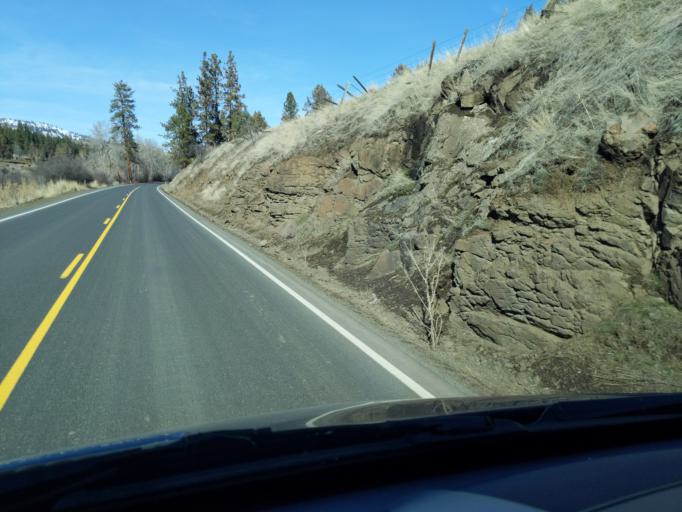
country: US
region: Oregon
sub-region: Grant County
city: John Day
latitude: 44.8519
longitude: -119.0304
